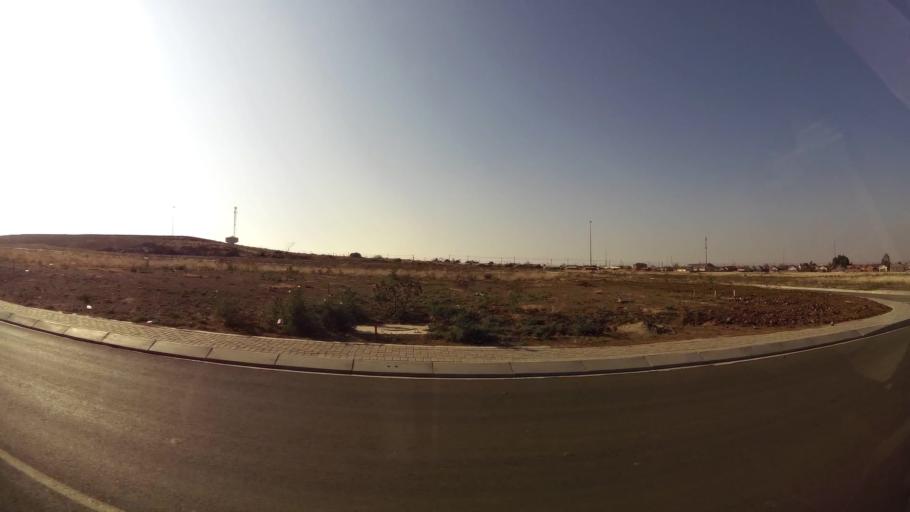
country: ZA
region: Orange Free State
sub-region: Mangaung Metropolitan Municipality
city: Bloemfontein
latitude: -29.1972
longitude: 26.2175
